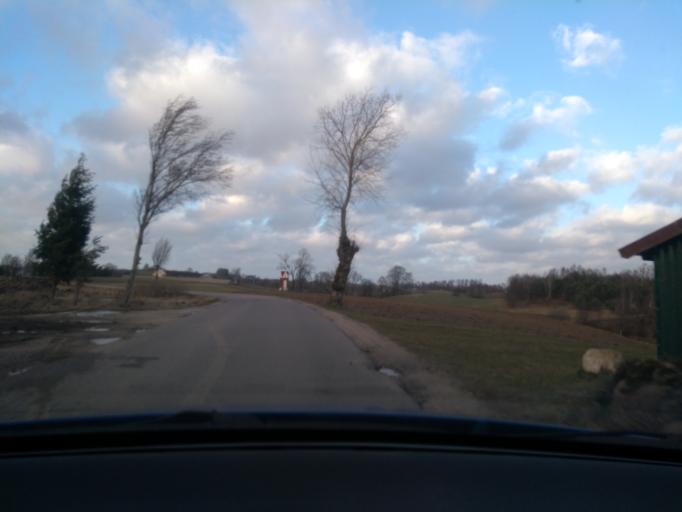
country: PL
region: Pomeranian Voivodeship
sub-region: Powiat kartuski
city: Kartuzy
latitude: 54.3739
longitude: 18.2159
